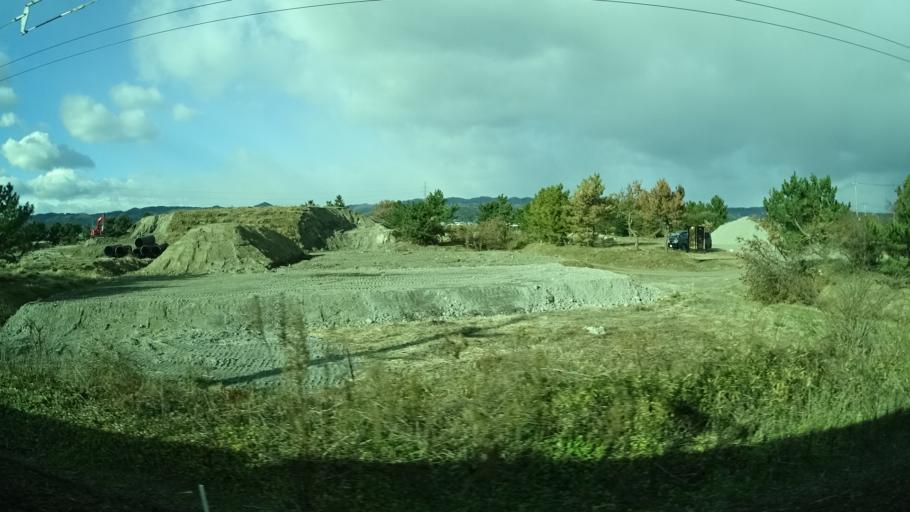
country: JP
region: Miyagi
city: Iwanuma
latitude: 38.1288
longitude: 140.8735
